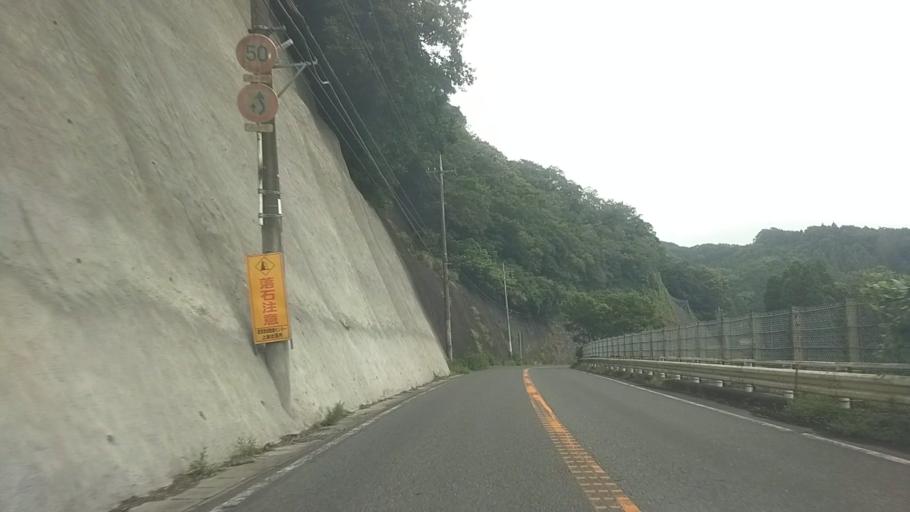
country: JP
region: Chiba
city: Kawaguchi
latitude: 35.2510
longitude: 140.0743
